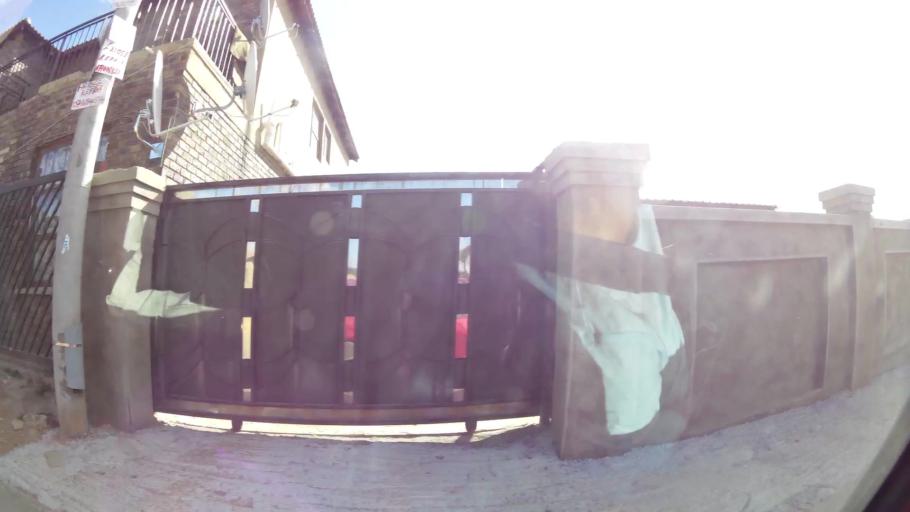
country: ZA
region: Gauteng
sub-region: City of Johannesburg Metropolitan Municipality
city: Modderfontein
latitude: -26.0392
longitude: 28.1773
